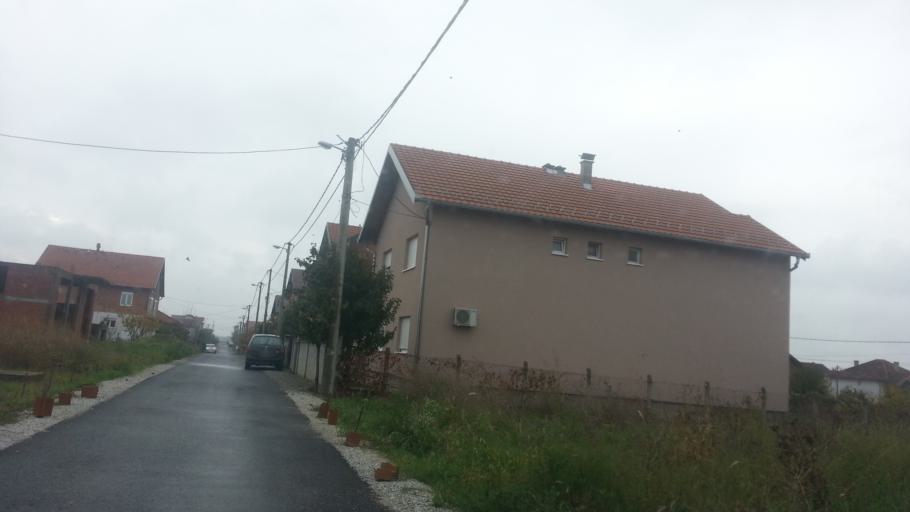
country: RS
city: Novi Banovci
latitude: 44.9086
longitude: 20.2945
